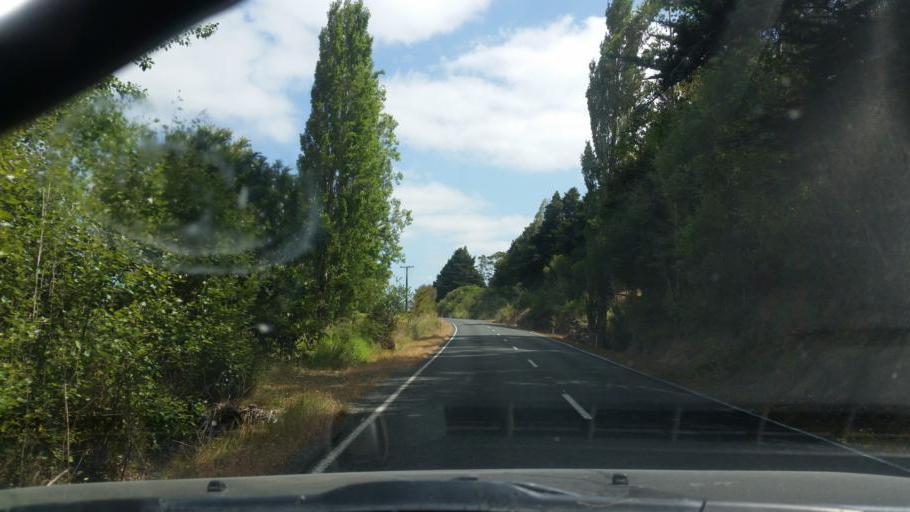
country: NZ
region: Northland
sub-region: Whangarei
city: Ruakaka
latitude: -35.9480
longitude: 174.2935
